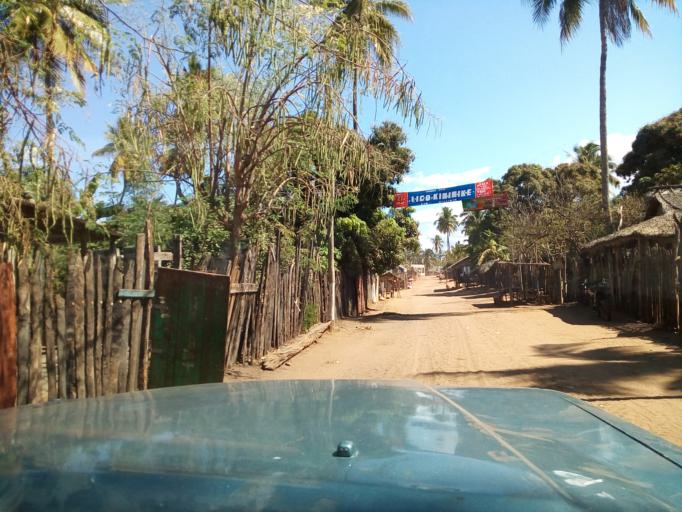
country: MG
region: Boeny
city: Mahajanga
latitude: -16.0110
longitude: 45.8679
